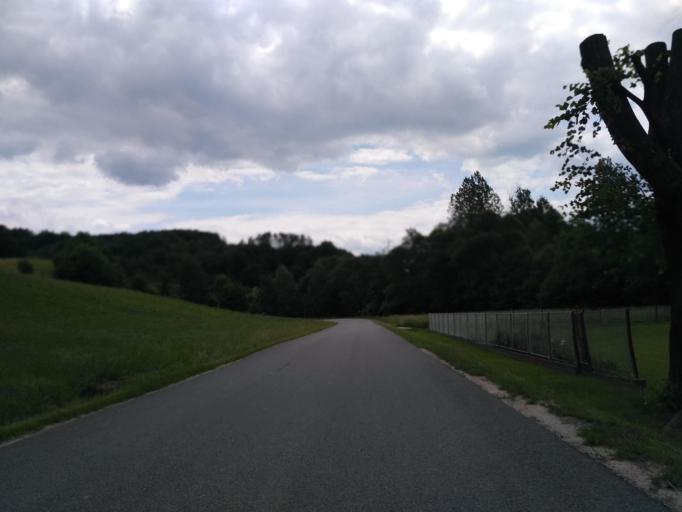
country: PL
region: Subcarpathian Voivodeship
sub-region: Powiat przeworski
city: Jawornik Polski
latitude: 49.8498
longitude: 22.3036
